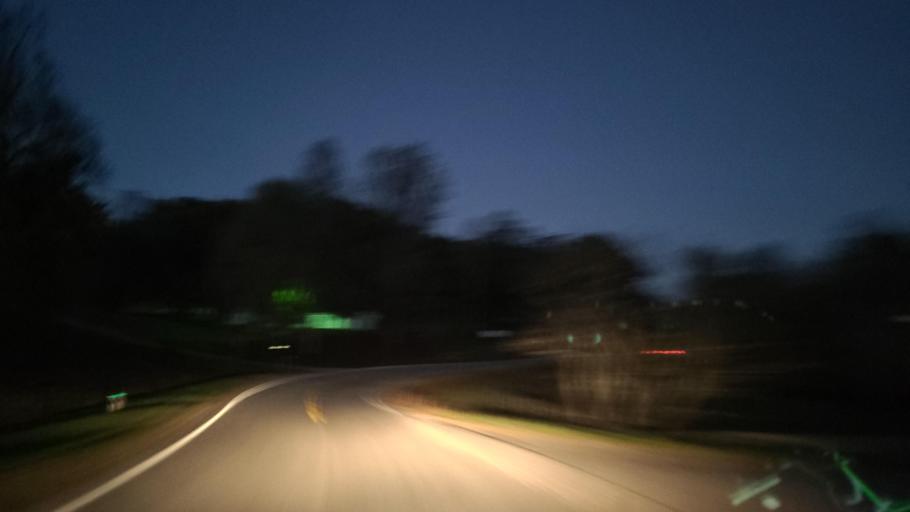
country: US
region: North Carolina
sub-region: Clay County
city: Hayesville
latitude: 34.9814
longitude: -83.8502
